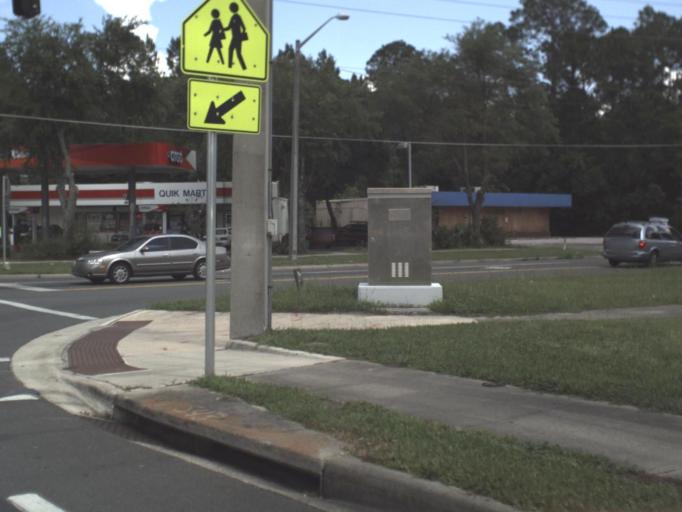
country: US
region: Florida
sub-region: Alachua County
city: Gainesville
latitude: 29.6883
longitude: -82.3061
